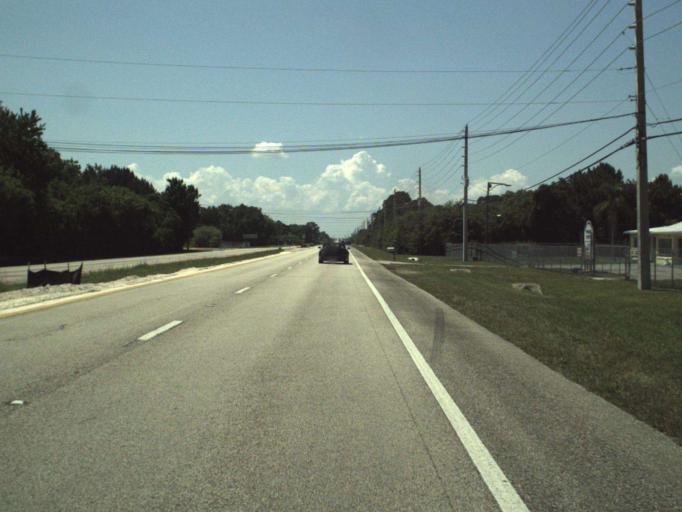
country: US
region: Florida
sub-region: Brevard County
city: Sharpes
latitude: 28.4305
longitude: -80.7080
